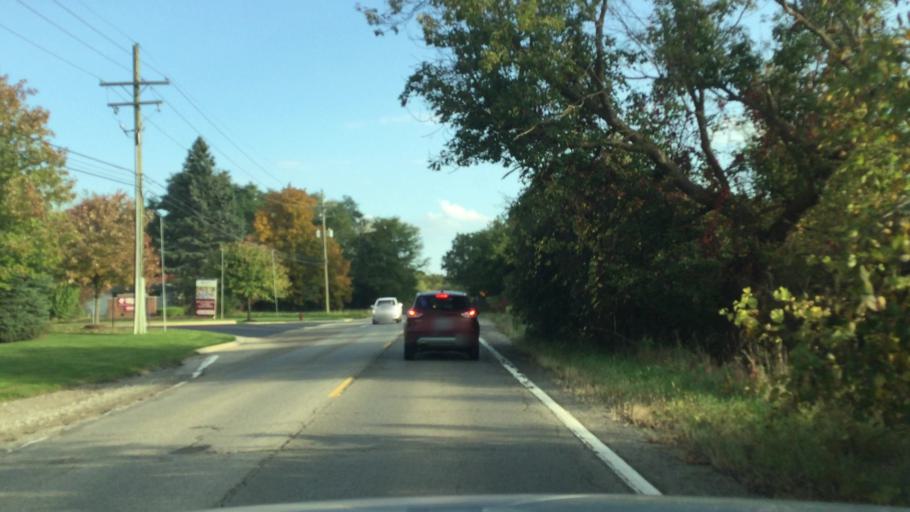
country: US
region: Michigan
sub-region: Oakland County
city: Wolverine Lake
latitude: 42.6250
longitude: -83.4564
